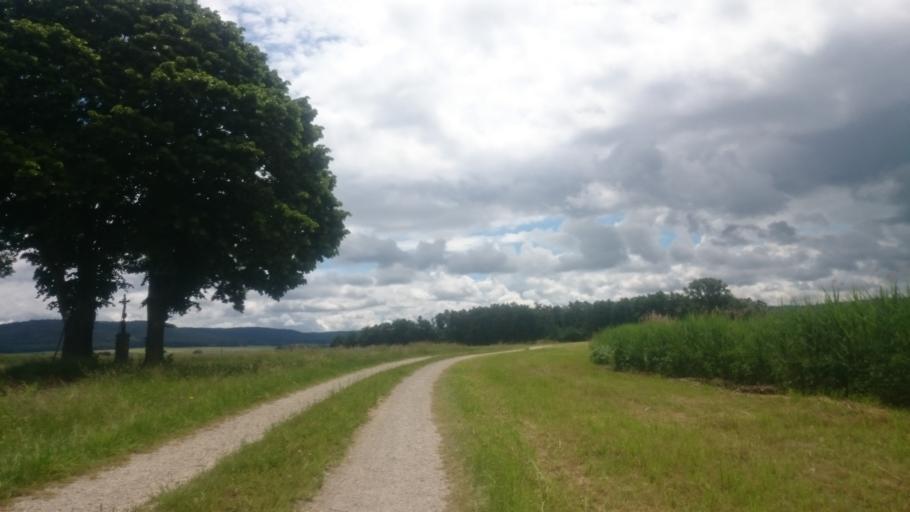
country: DE
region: Bavaria
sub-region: Upper Palatinate
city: Freystadt
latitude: 49.1546
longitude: 11.3186
